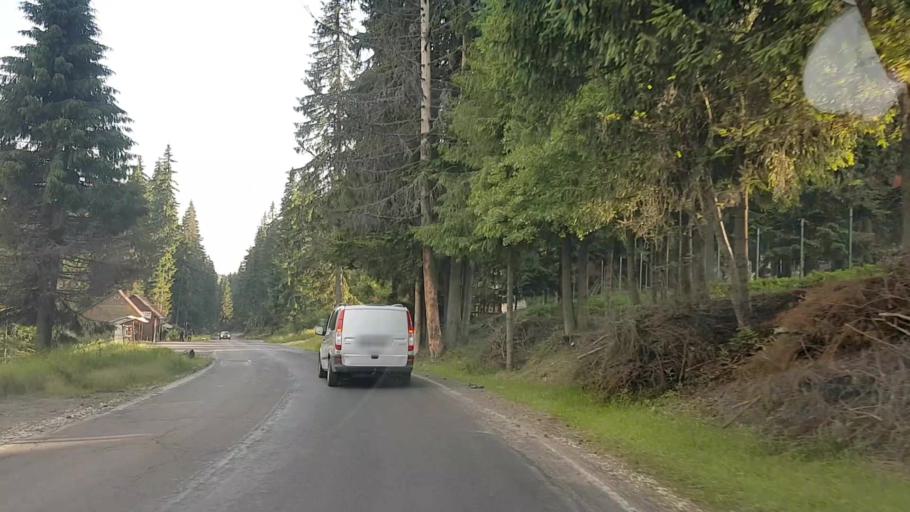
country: RO
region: Harghita
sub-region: Comuna Varsag
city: Varsag
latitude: 46.6551
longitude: 25.2931
